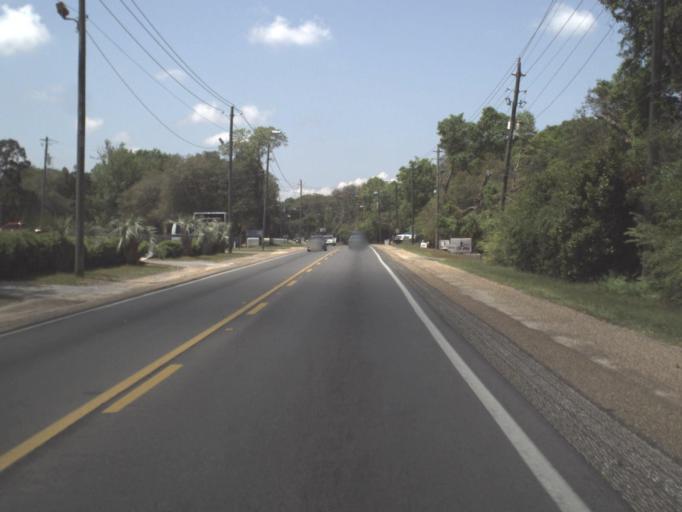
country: US
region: Florida
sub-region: Escambia County
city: Myrtle Grove
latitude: 30.4318
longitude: -87.3021
